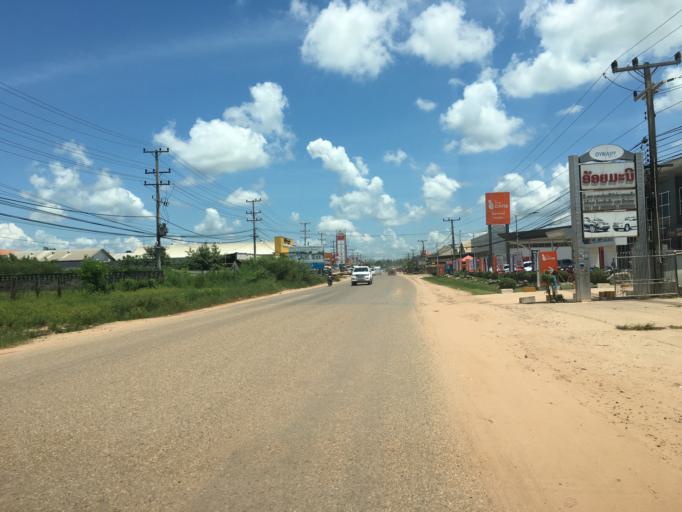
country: LA
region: Vientiane
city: Vientiane
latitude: 18.0241
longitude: 102.5473
